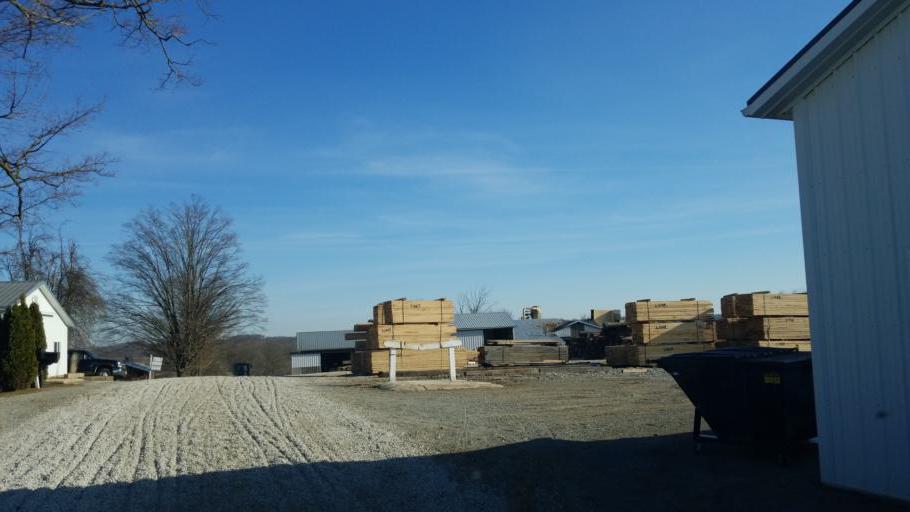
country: US
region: Ohio
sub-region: Knox County
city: Fredericktown
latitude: 40.5342
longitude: -82.6141
